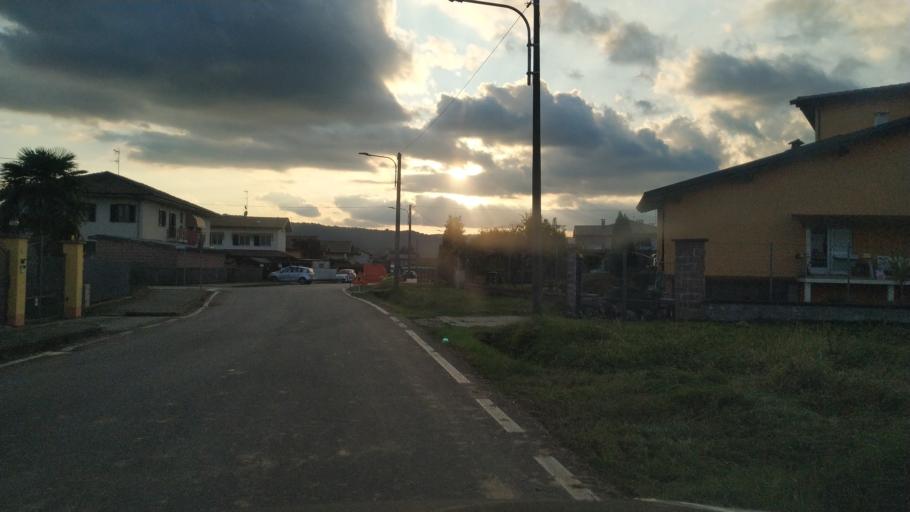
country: IT
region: Piedmont
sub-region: Provincia di Biella
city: Vergnasco
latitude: 45.4745
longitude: 8.0897
